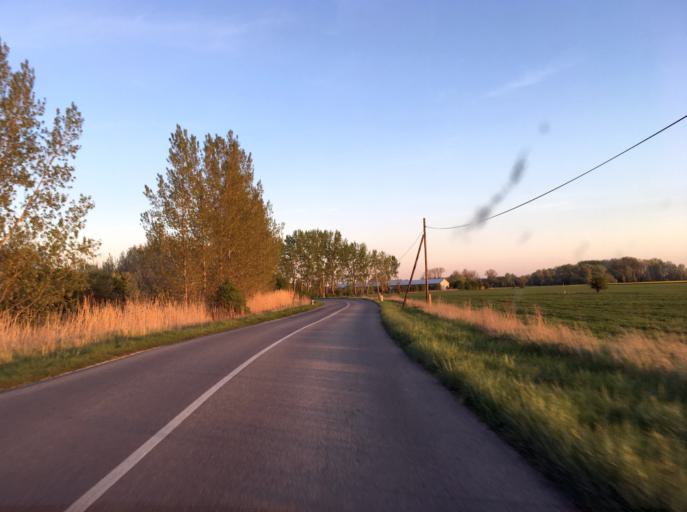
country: SK
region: Nitriansky
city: Kolarovo
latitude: 47.8764
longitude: 17.9146
